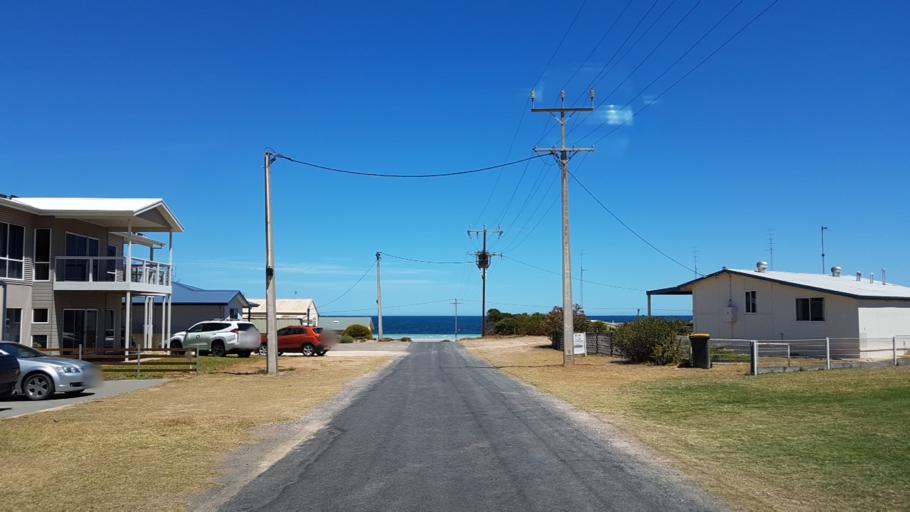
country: AU
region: South Australia
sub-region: Copper Coast
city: Wallaroo
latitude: -33.8975
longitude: 137.6295
